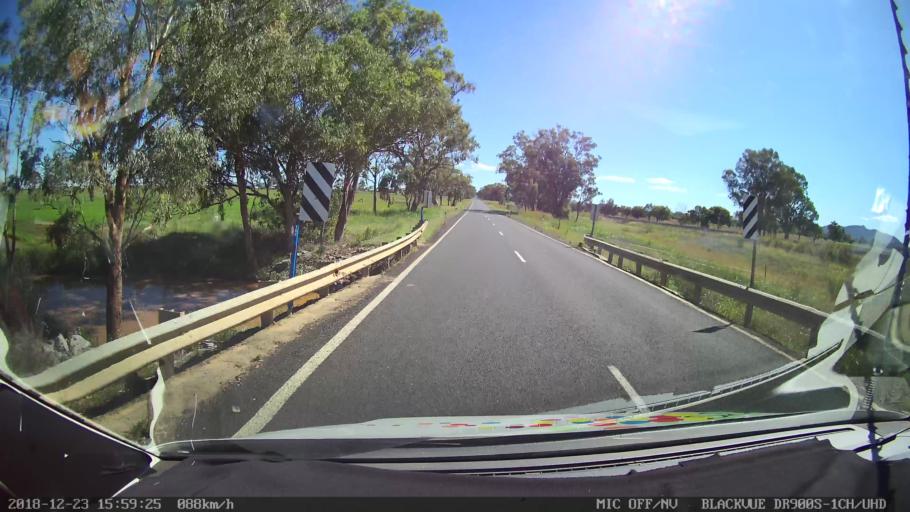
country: AU
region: New South Wales
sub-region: Tamworth Municipality
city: Phillip
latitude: -31.1995
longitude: 150.8334
